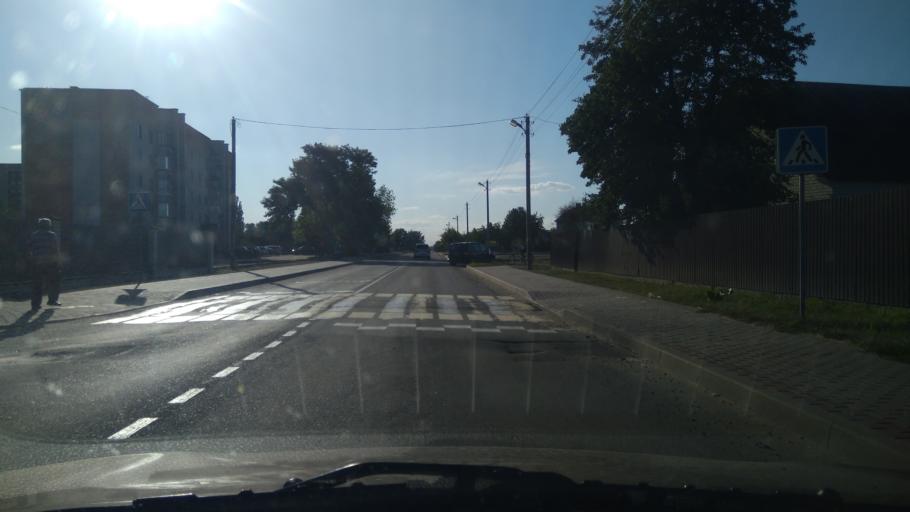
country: BY
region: Brest
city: Byaroza
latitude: 52.5409
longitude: 24.9766
